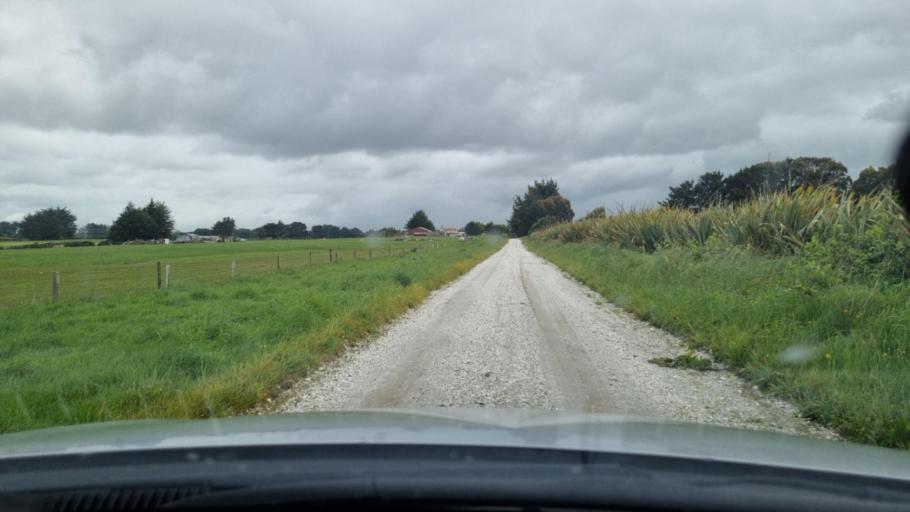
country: NZ
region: Southland
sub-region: Invercargill City
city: Invercargill
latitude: -46.4503
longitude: 168.3939
